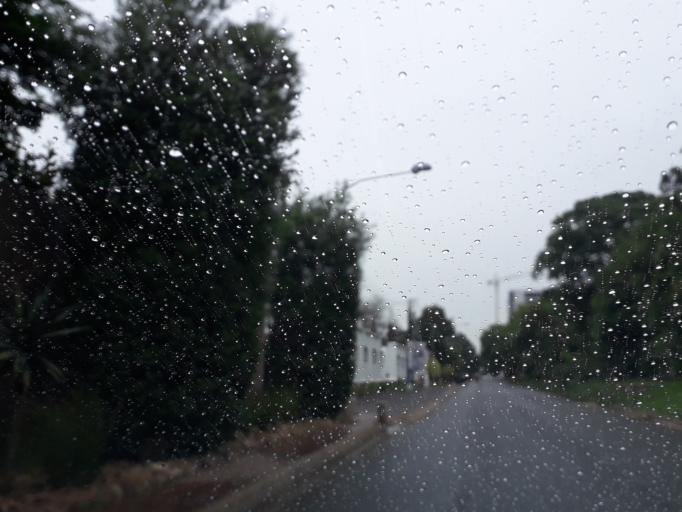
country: ZA
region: Gauteng
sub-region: City of Johannesburg Metropolitan Municipality
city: Johannesburg
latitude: -26.1264
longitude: 28.0463
